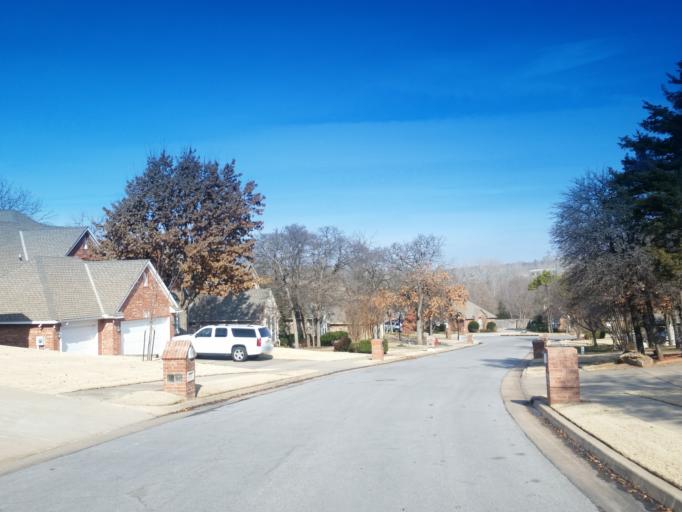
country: US
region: Oklahoma
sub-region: Oklahoma County
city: Edmond
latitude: 35.6463
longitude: -97.4321
